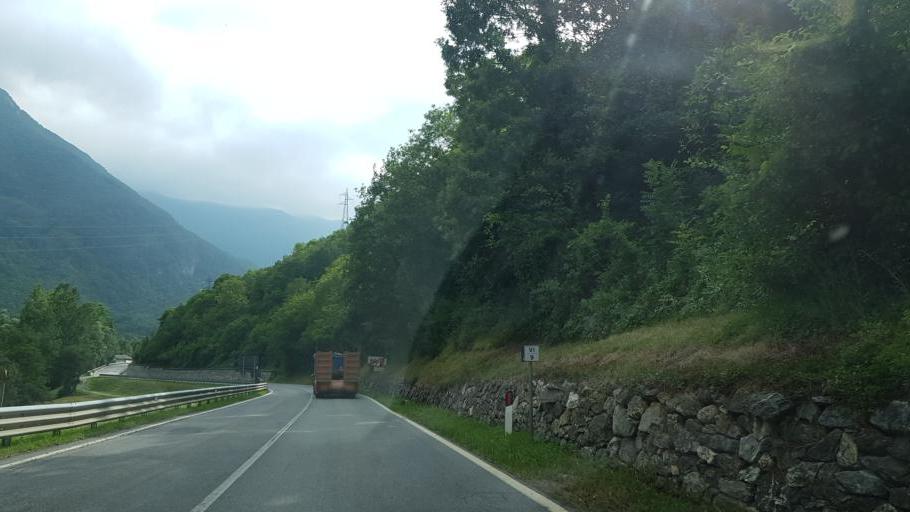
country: IT
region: Piedmont
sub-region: Provincia di Cuneo
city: Moiola
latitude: 44.3180
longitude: 7.3875
